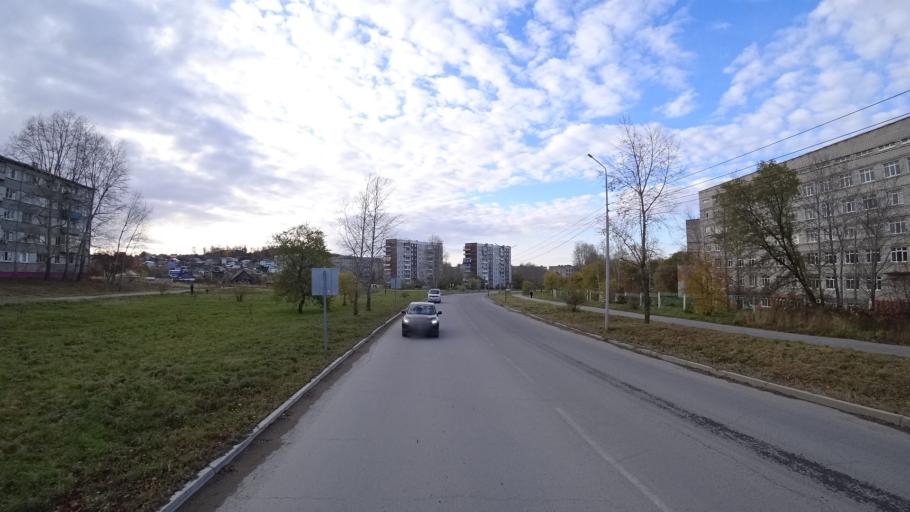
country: RU
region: Khabarovsk Krai
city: Amursk
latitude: 50.2357
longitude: 136.9112
